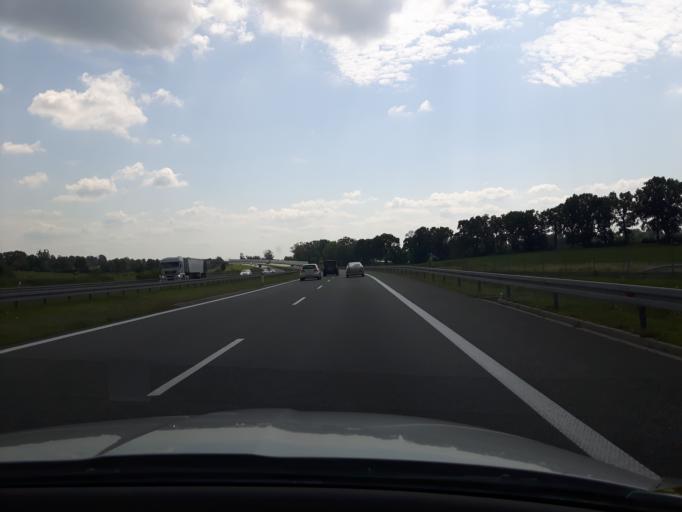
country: PL
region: Warmian-Masurian Voivodeship
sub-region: Powiat ostrodzki
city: Milomlyn
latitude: 53.7883
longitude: 19.7981
